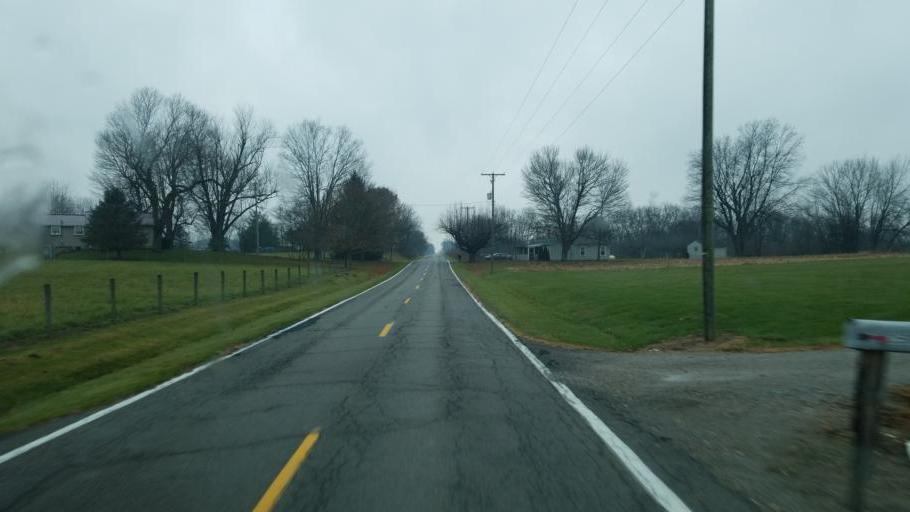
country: US
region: Ohio
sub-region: Licking County
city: Utica
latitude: 40.2597
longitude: -82.5634
